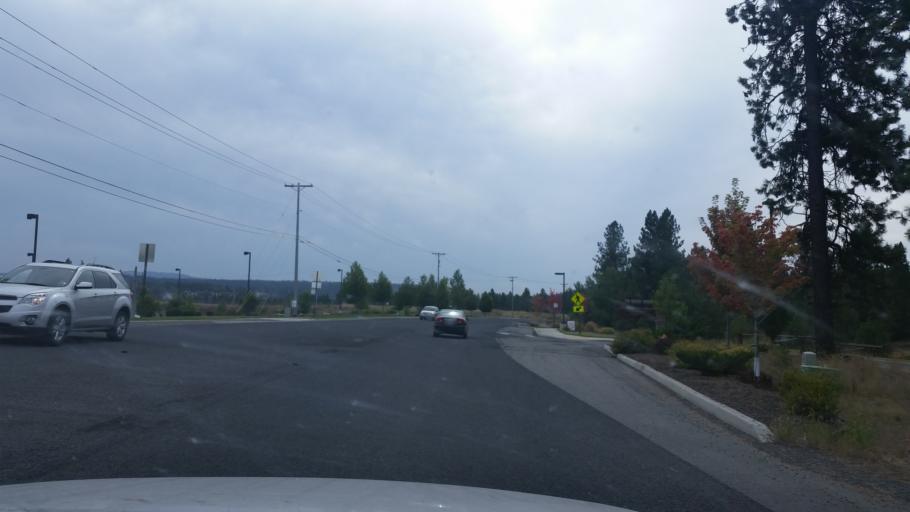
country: US
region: Washington
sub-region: Spokane County
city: Spokane
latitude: 47.6676
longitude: -117.4703
